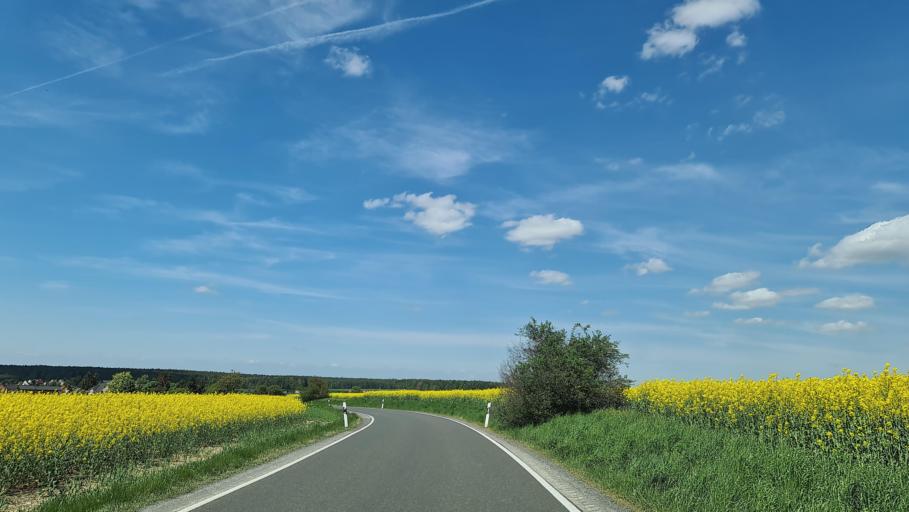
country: DE
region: Saxony
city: Pausa
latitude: 50.6175
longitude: 12.0396
